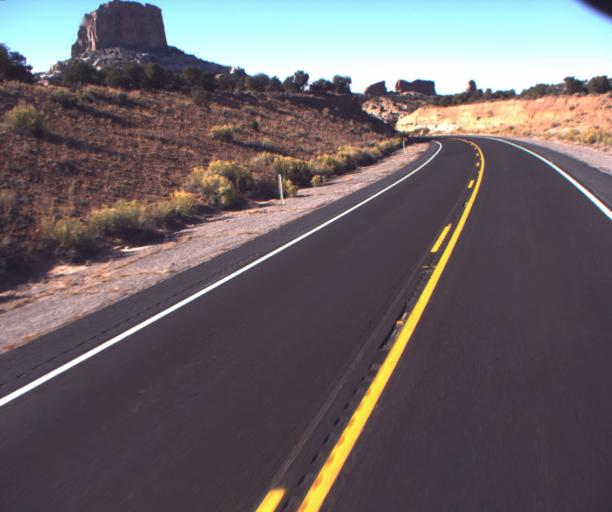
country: US
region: Arizona
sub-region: Coconino County
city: Kaibito
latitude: 36.5997
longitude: -110.9136
